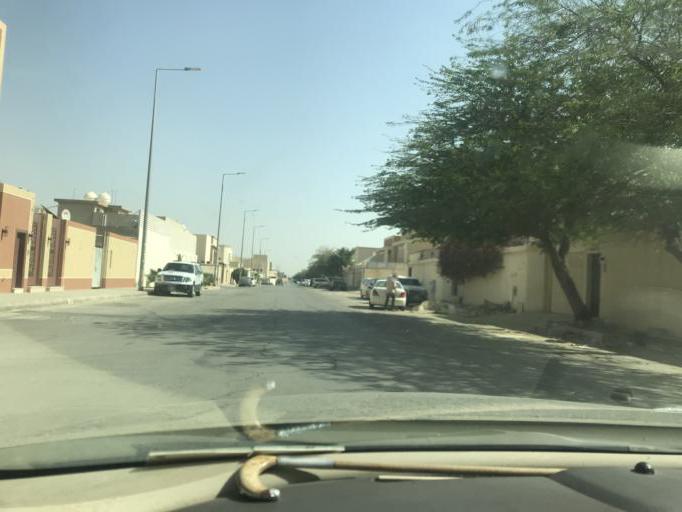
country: SA
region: Ar Riyad
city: Riyadh
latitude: 24.7367
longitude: 46.7628
